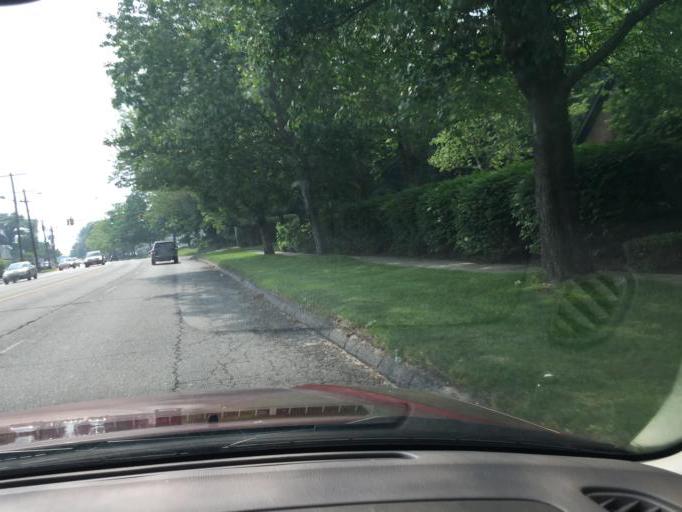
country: US
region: Connecticut
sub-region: Fairfield County
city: Westport
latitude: 41.1391
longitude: -73.3269
